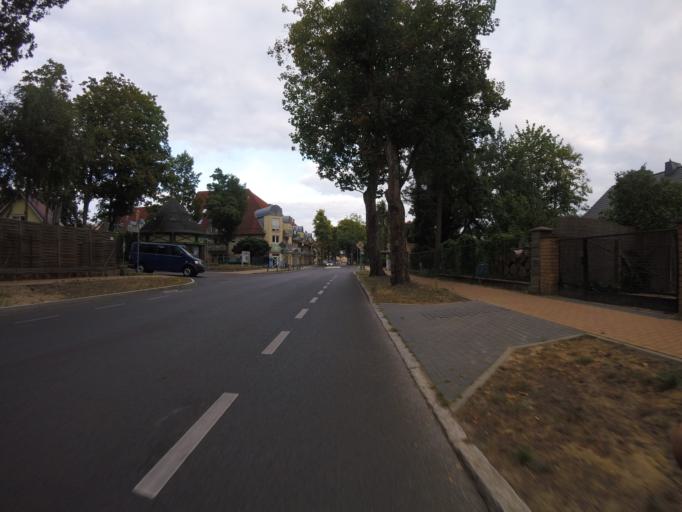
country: DE
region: Brandenburg
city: Birkenwerder
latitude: 52.6739
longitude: 13.3159
